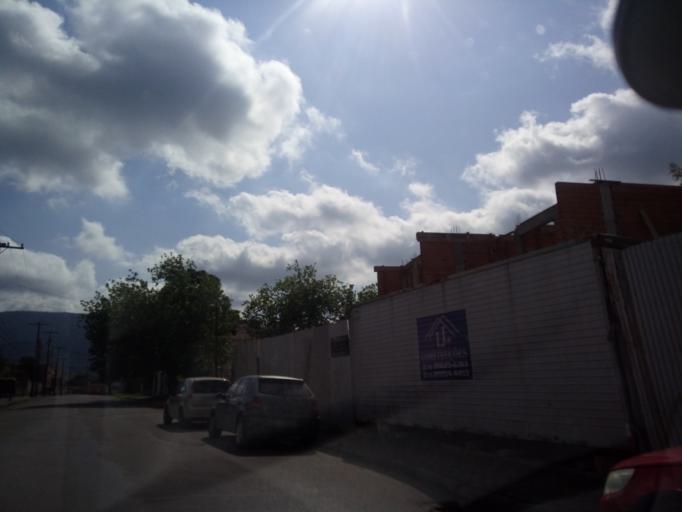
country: BR
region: Rio Grande do Sul
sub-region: Santa Maria
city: Santa Maria
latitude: -29.7009
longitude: -53.7127
